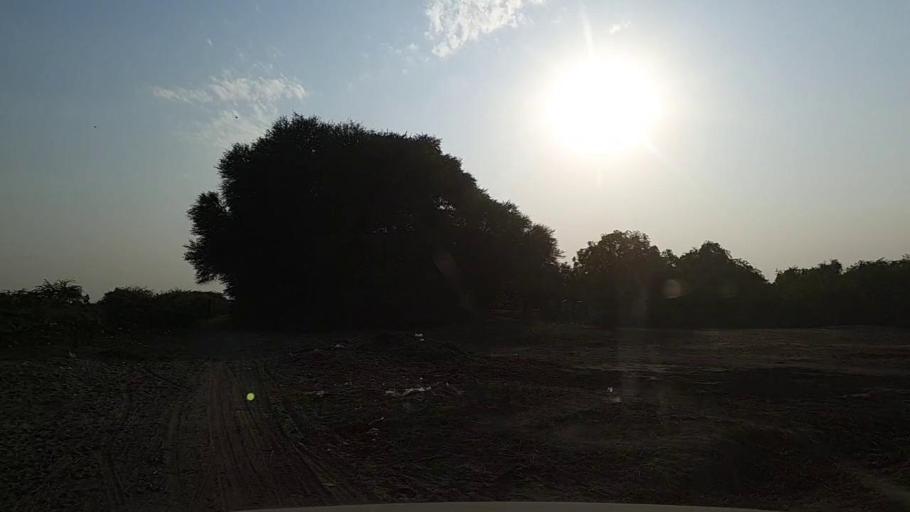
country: PK
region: Sindh
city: Daro Mehar
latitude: 24.7771
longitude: 68.1949
